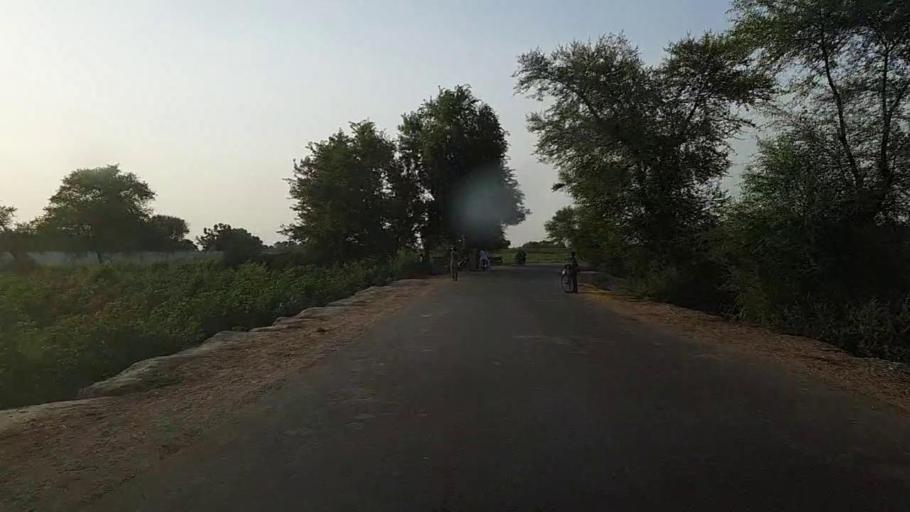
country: PK
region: Sindh
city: Ubauro
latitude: 28.1737
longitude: 69.8294
